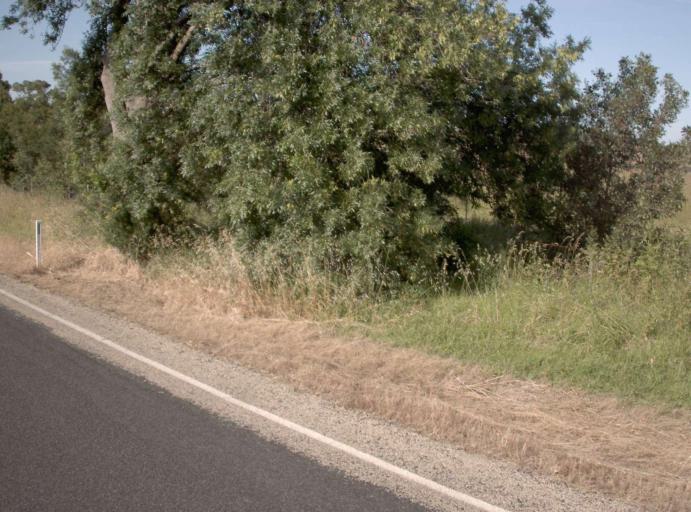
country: AU
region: Victoria
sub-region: East Gippsland
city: Lakes Entrance
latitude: -37.8467
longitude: 147.8508
